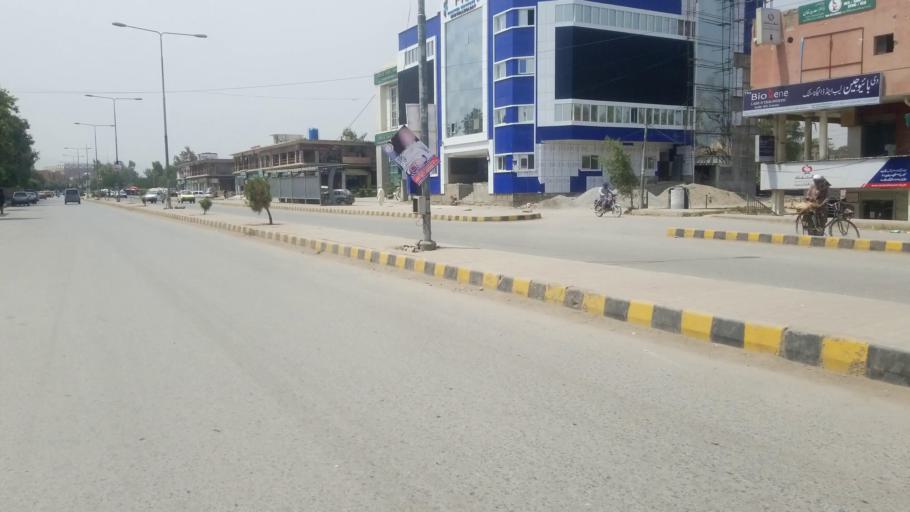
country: PK
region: Khyber Pakhtunkhwa
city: Peshawar
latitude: 33.9939
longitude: 71.4521
